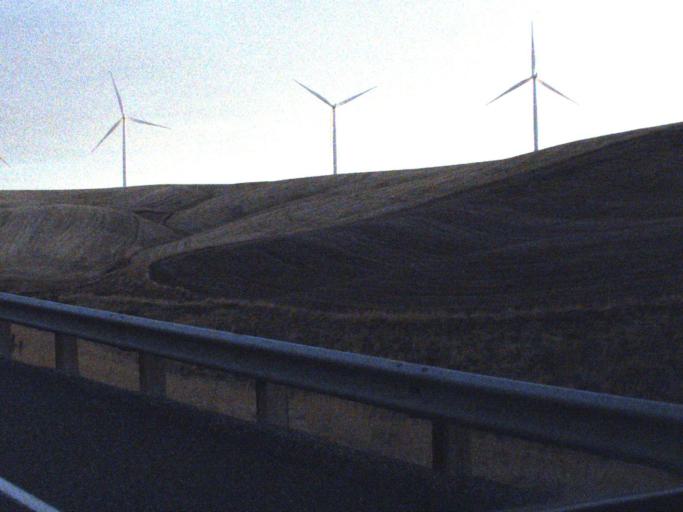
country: US
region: Washington
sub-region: Garfield County
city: Pomeroy
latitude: 46.5459
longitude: -117.7751
